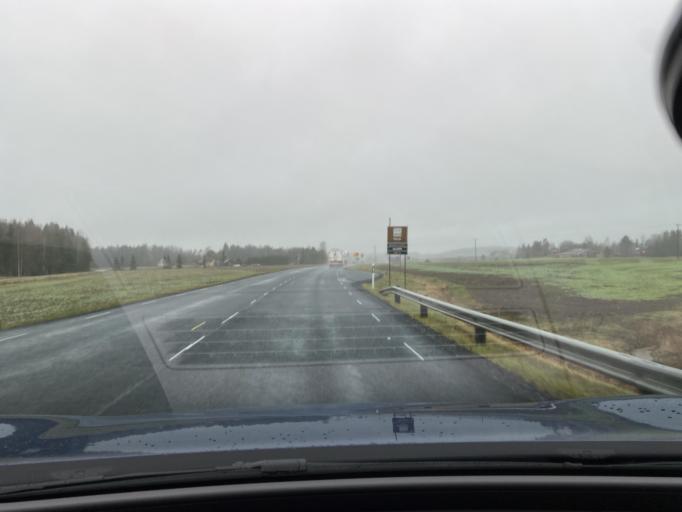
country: FI
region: Haeme
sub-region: Forssa
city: Ypaejae
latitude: 60.7779
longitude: 23.3139
